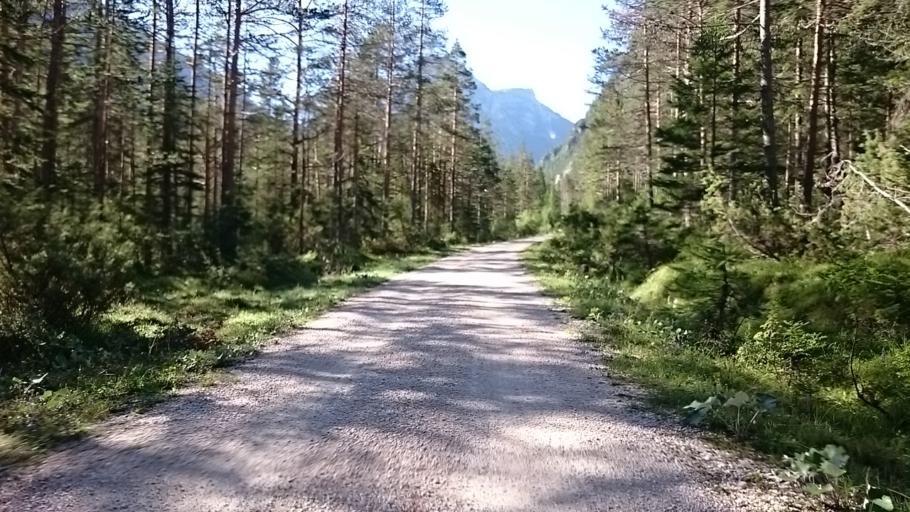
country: IT
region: Trentino-Alto Adige
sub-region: Bolzano
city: Dobbiaco
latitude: 46.6536
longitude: 12.2267
